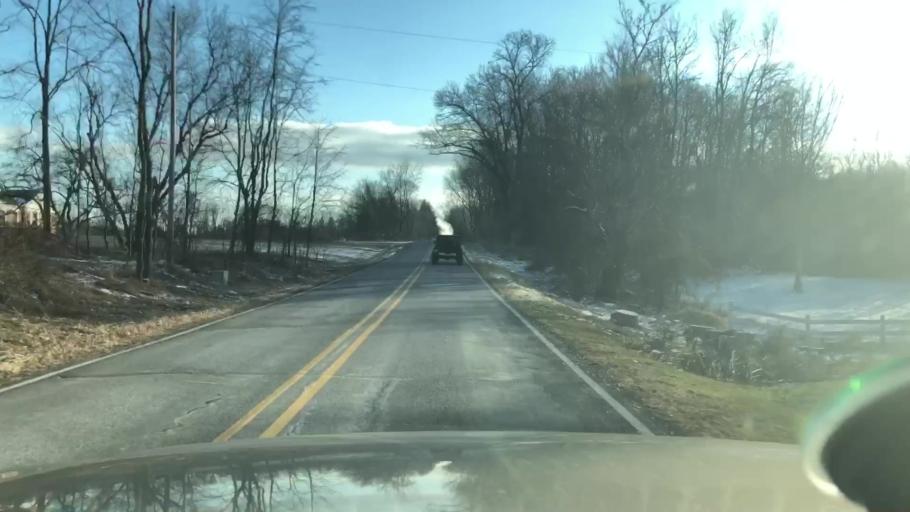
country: US
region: Michigan
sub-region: Jackson County
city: Vandercook Lake
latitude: 42.1262
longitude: -84.4515
